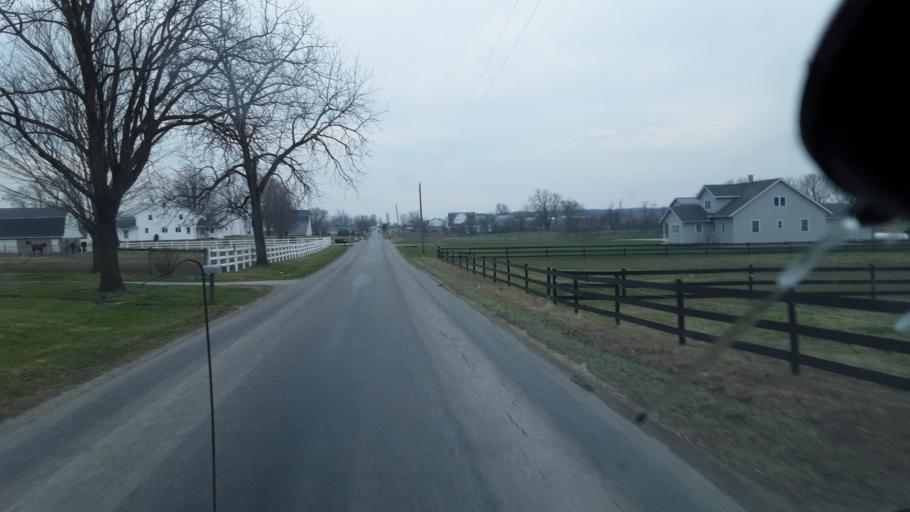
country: US
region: Indiana
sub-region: Elkhart County
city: Middlebury
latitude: 41.6830
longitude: -85.6197
